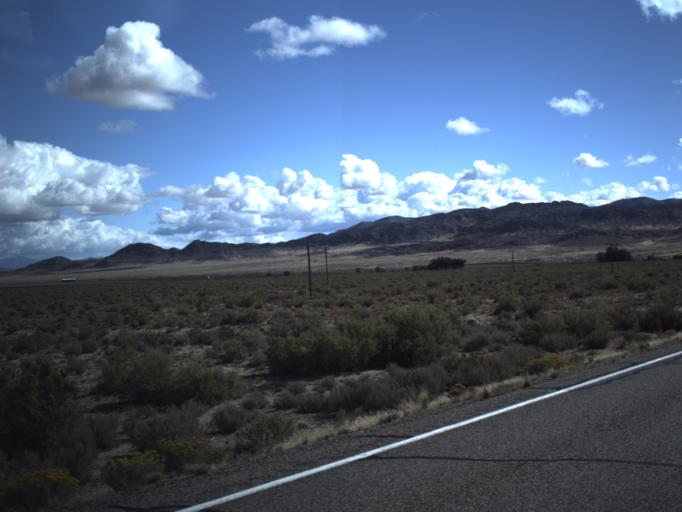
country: US
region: Nevada
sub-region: White Pine County
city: McGill
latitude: 38.9449
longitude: -114.0405
